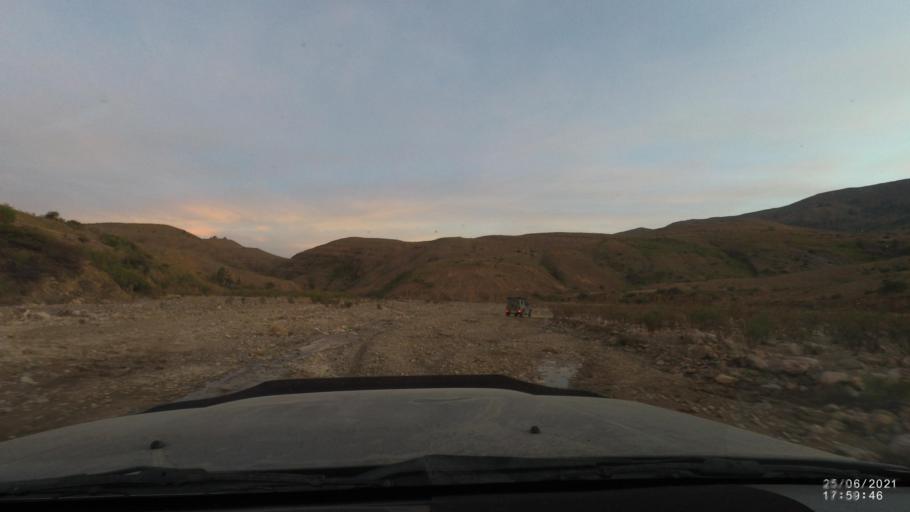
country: BO
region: Cochabamba
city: Mizque
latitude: -17.9448
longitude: -65.6346
